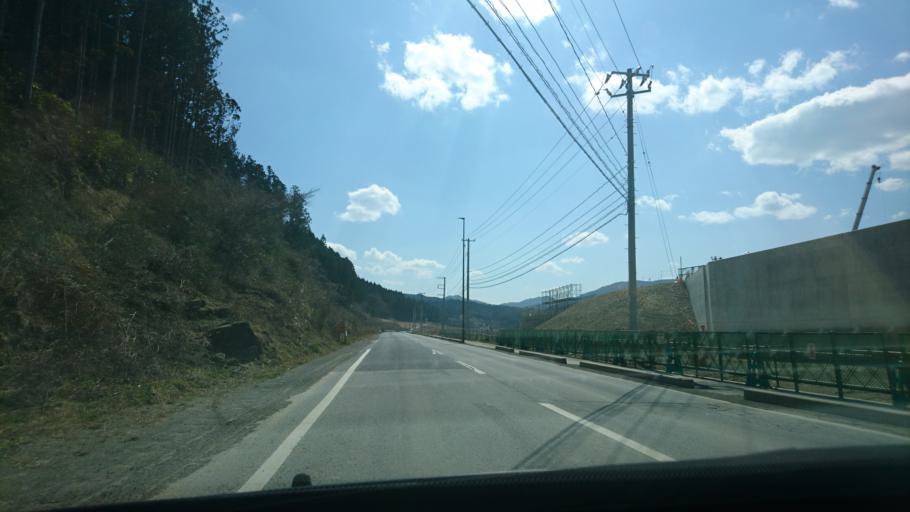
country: JP
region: Miyagi
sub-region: Oshika Gun
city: Onagawa Cho
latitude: 38.6405
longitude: 141.4613
